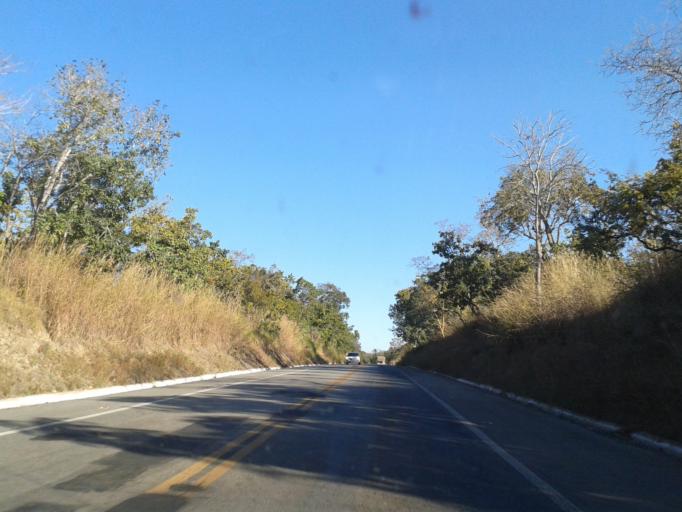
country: BR
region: Goias
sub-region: Itapuranga
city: Itapuranga
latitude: -15.5478
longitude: -50.2883
